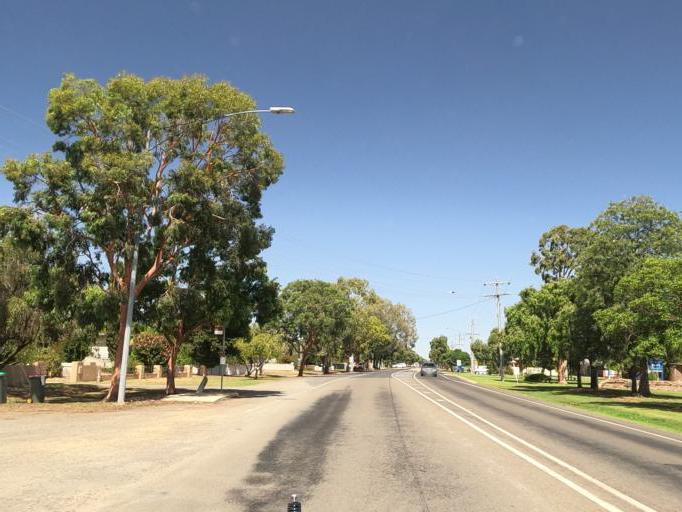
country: AU
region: Victoria
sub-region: Moira
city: Yarrawonga
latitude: -36.0152
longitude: 146.0127
